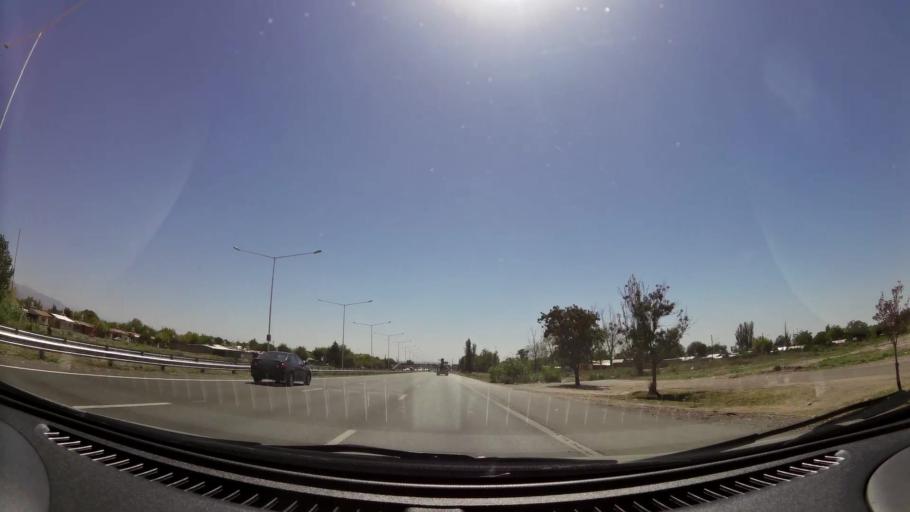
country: AR
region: Mendoza
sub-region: Departamento de Godoy Cruz
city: Godoy Cruz
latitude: -32.9601
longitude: -68.8377
